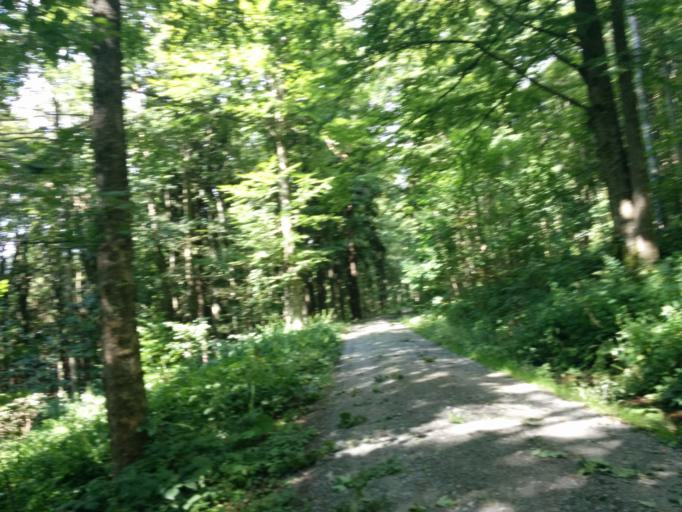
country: AT
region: Upper Austria
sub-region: Politischer Bezirk Rohrbach
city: Ulrichsberg
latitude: 48.7143
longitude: 13.9360
